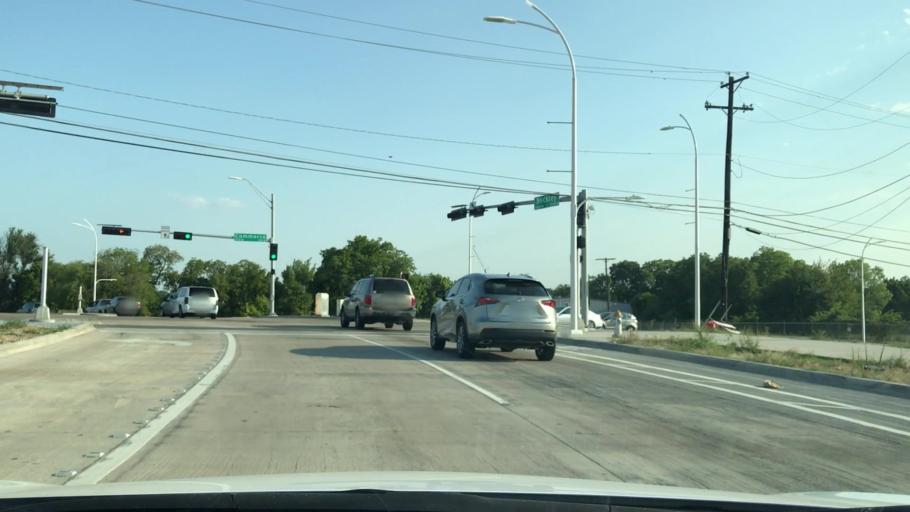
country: US
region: Texas
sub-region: Dallas County
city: Dallas
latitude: 32.7751
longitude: -96.8237
